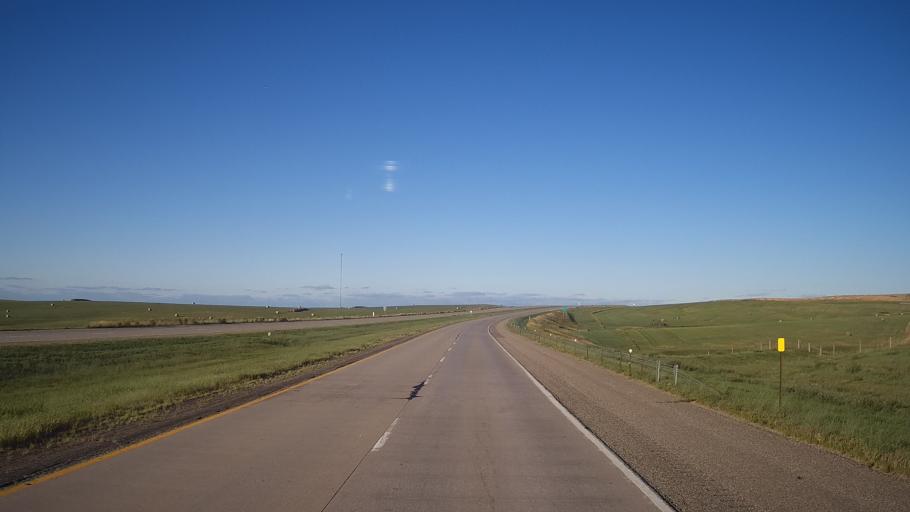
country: US
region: South Dakota
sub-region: Jackson County
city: Kadoka
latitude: 43.8938
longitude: -101.1160
